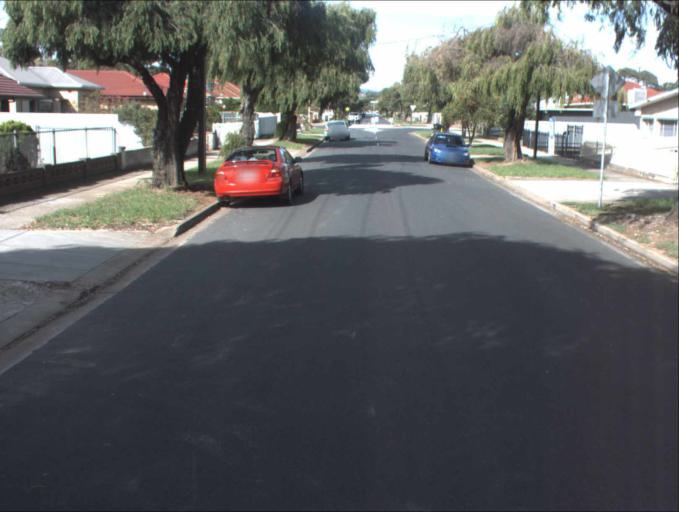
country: AU
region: South Australia
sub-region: Port Adelaide Enfield
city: Blair Athol
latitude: -34.8635
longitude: 138.5842
